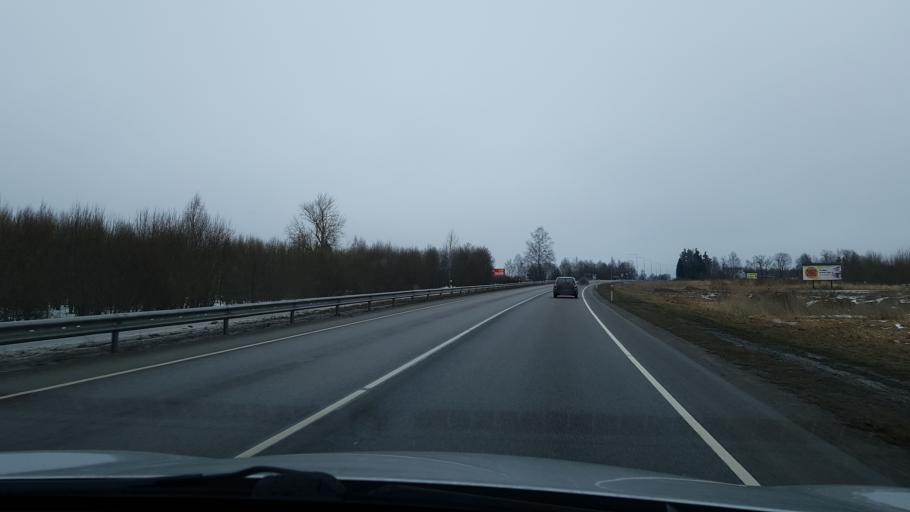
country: EE
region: Tartu
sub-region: UElenurme vald
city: Ulenurme
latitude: 58.3371
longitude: 26.6504
